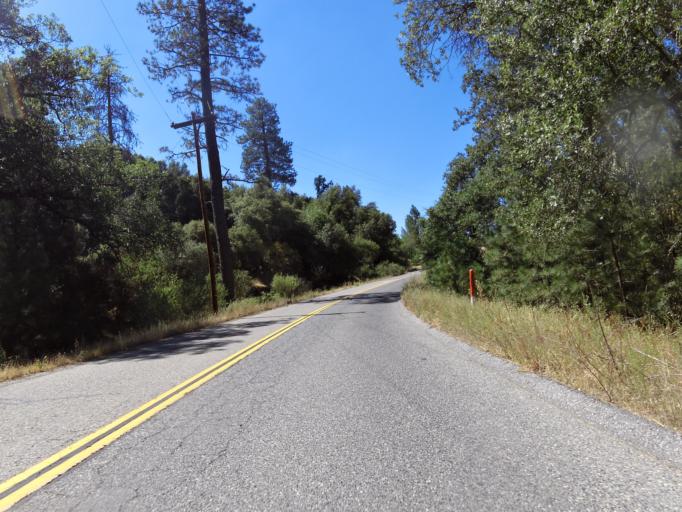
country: US
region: California
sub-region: Madera County
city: Ahwahnee
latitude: 37.3571
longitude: -119.6857
